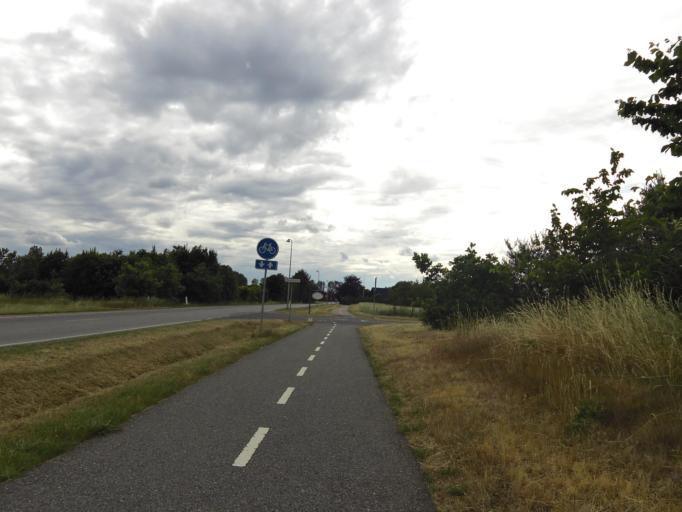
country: DK
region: South Denmark
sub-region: Esbjerg Kommune
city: Ribe
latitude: 55.3346
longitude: 8.7894
